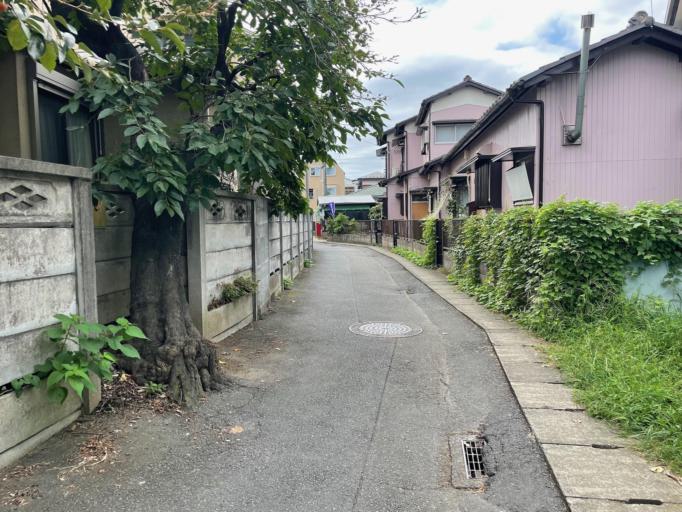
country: JP
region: Tokyo
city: Chofugaoka
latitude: 35.6220
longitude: 139.5620
